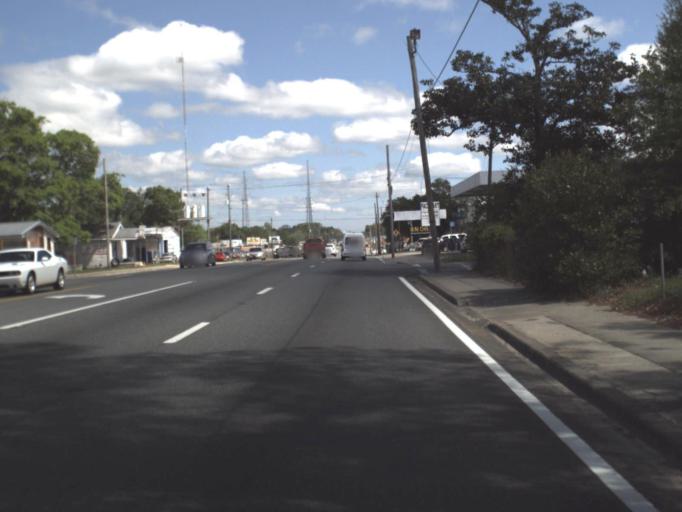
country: US
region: Florida
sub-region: Escambia County
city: Pensacola
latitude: 30.4258
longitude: -87.2409
